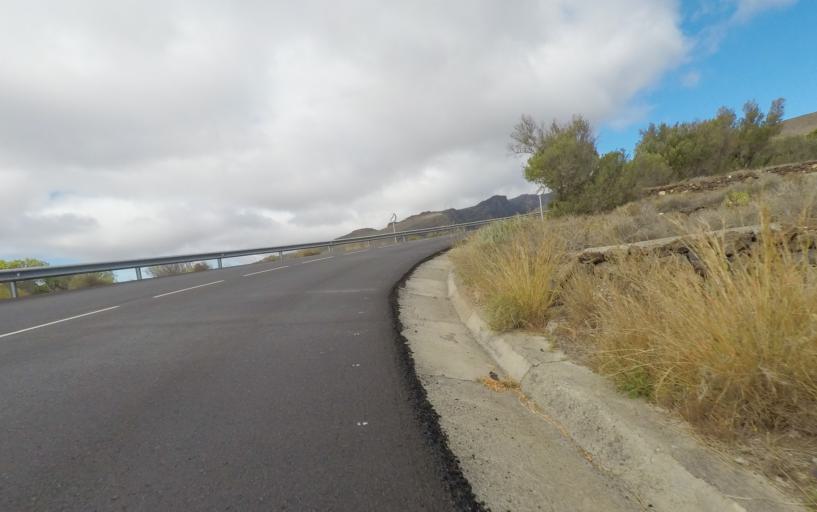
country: ES
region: Canary Islands
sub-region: Provincia de Santa Cruz de Tenerife
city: Alajero
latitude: 28.0487
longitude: -17.1980
